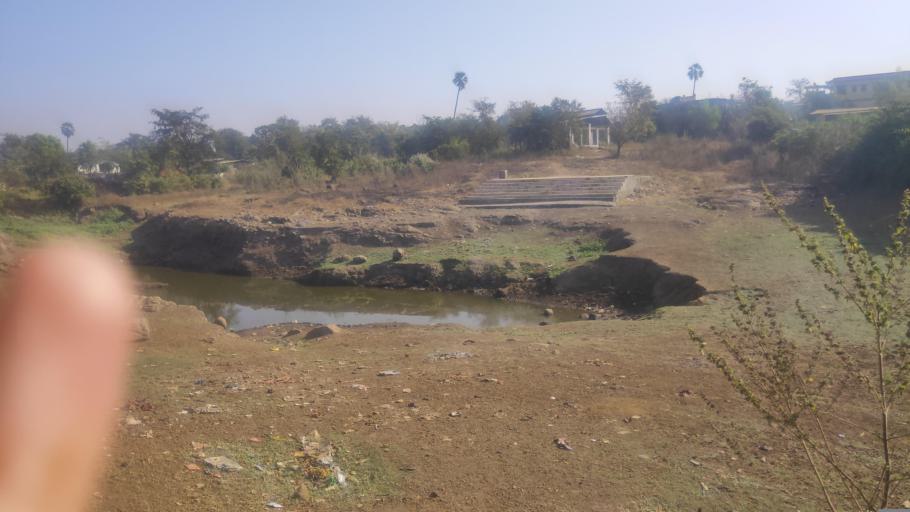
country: IN
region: Maharashtra
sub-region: Thane
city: Bhiwandi
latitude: 19.3068
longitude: 73.0148
